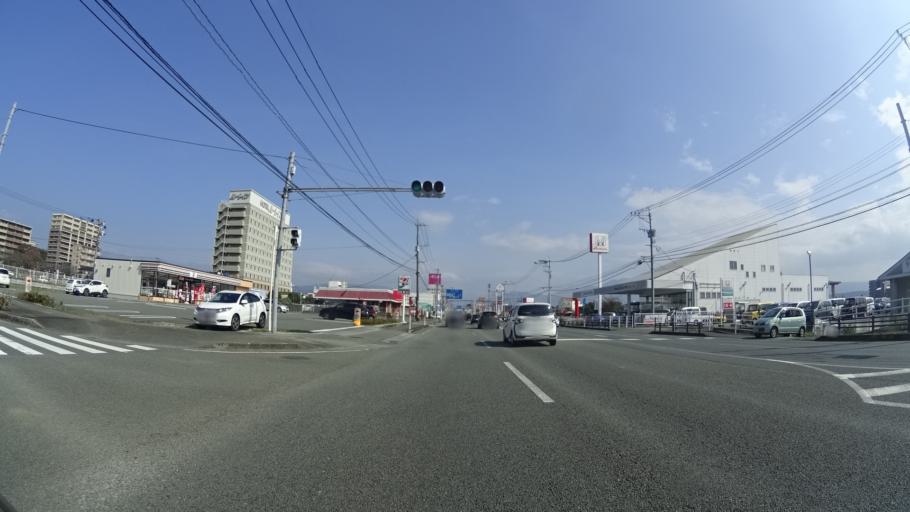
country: JP
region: Kumamoto
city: Ozu
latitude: 32.8756
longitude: 130.8633
